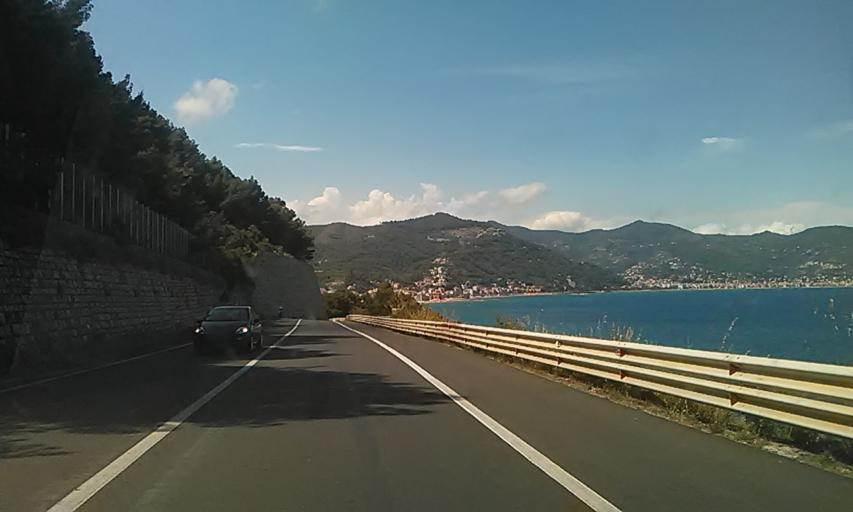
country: IT
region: Liguria
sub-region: Provincia di Savona
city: Laigueglia
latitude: 43.9643
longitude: 8.1664
